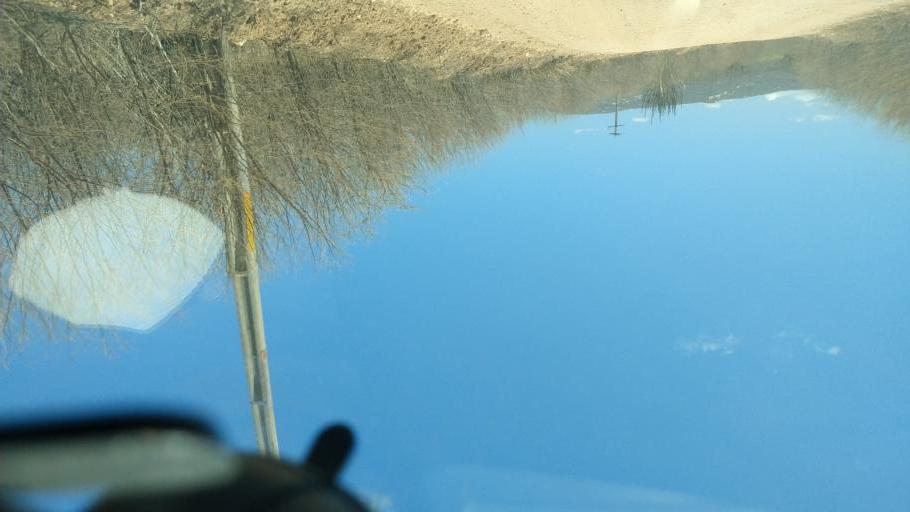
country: BR
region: Rio Grande do Norte
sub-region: Cerro Cora
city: Cerro Cora
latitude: -6.0099
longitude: -36.2908
